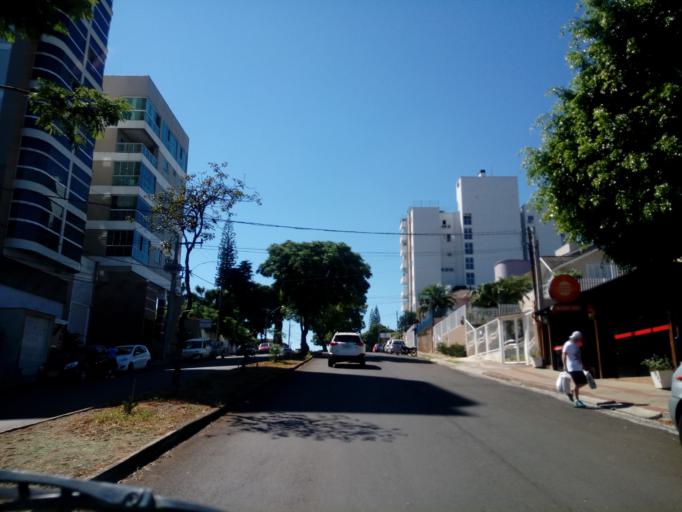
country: BR
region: Santa Catarina
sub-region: Chapeco
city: Chapeco
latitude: -27.1053
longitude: -52.6254
